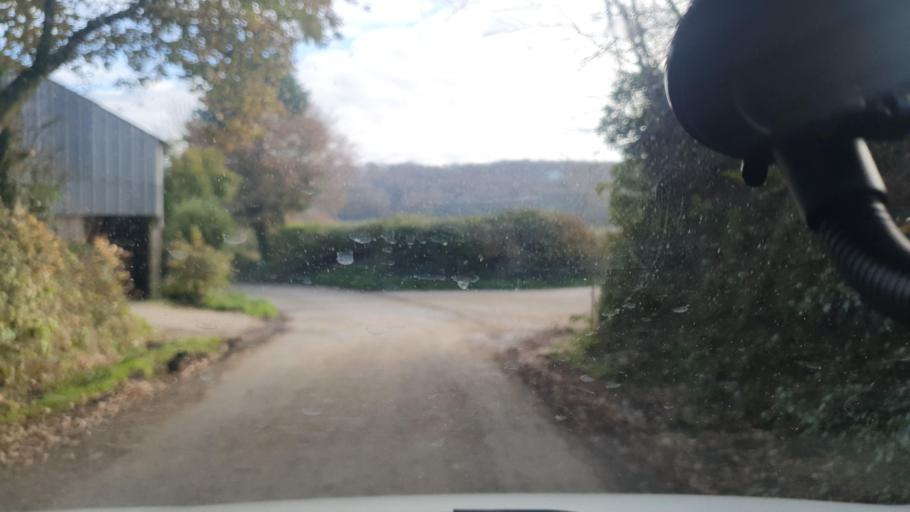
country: FR
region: Brittany
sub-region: Departement du Finistere
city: Landrevarzec
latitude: 48.1054
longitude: -4.0417
